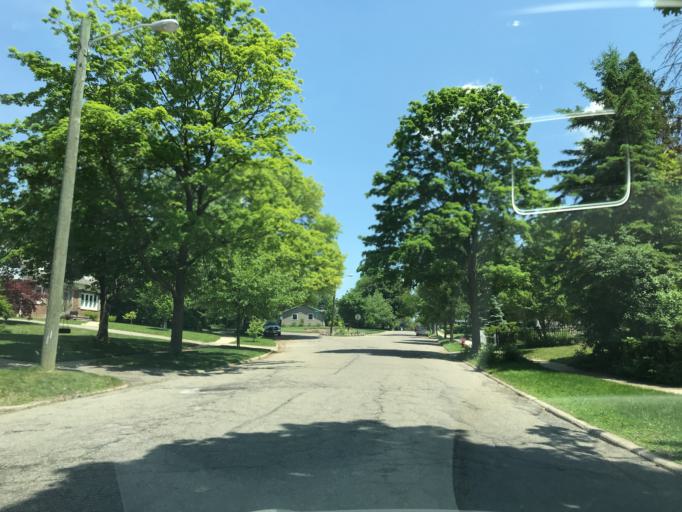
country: US
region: Michigan
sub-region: Washtenaw County
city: Ann Arbor
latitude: 42.2589
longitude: -83.7216
